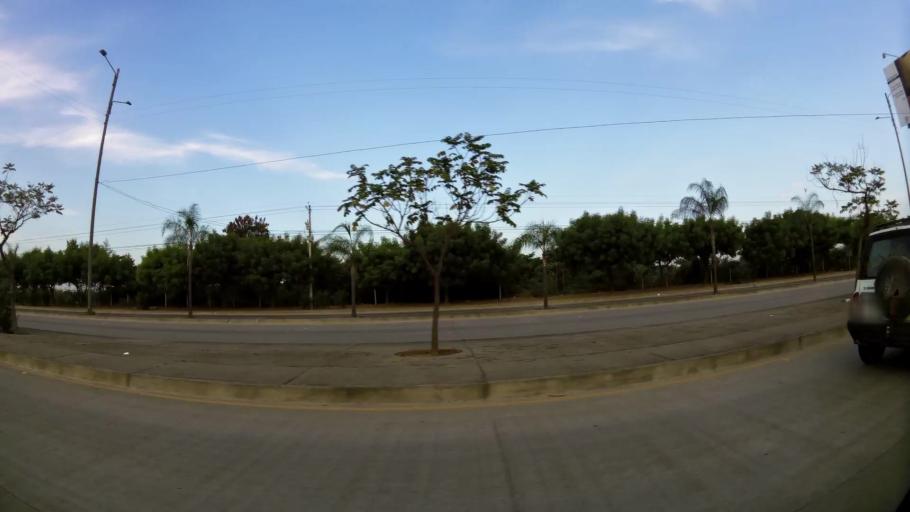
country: EC
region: Guayas
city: Eloy Alfaro
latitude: -2.0960
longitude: -79.8925
